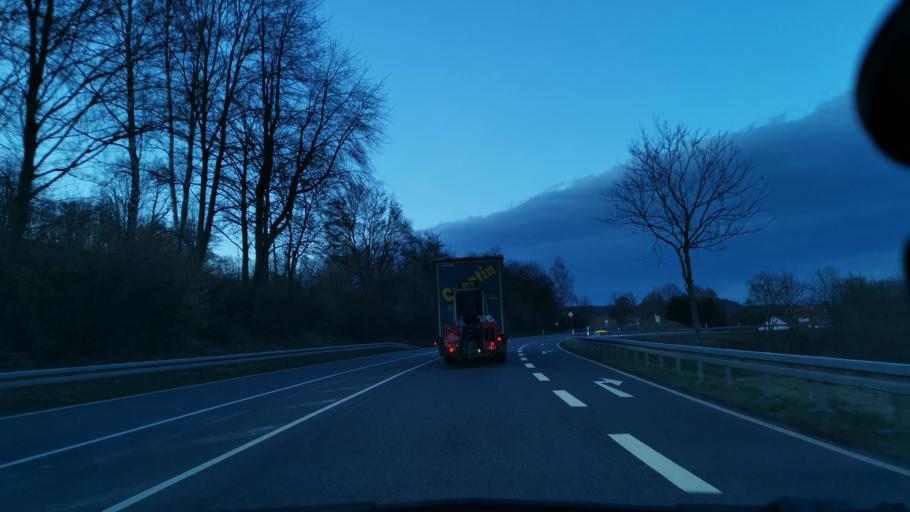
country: DE
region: Hesse
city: Bebra
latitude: 51.0039
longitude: 9.8134
